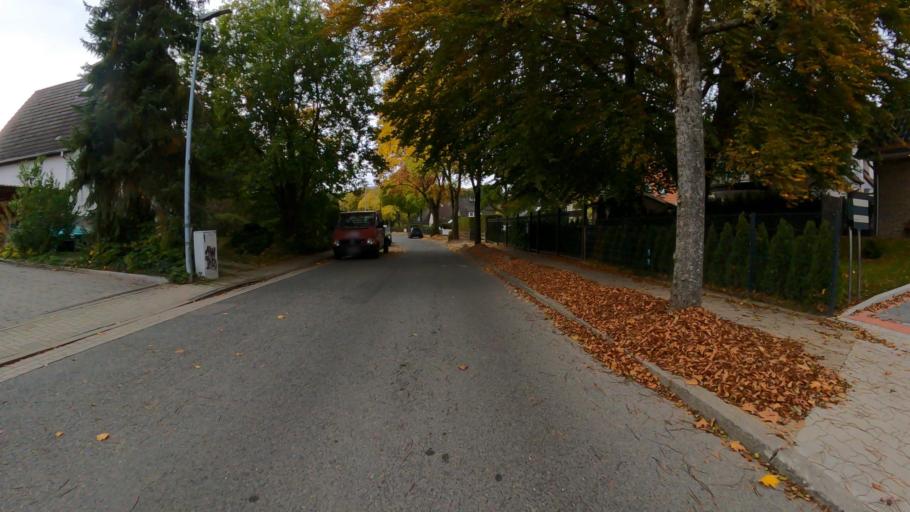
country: DE
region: Schleswig-Holstein
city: Ahrensburg
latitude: 53.6570
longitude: 10.2449
